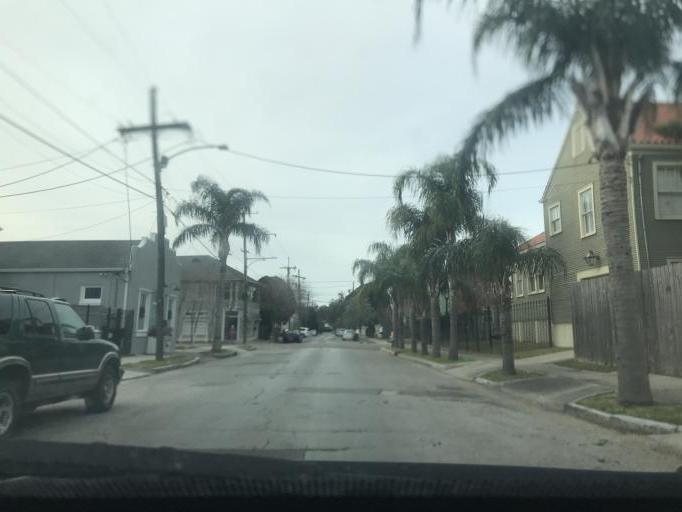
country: US
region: Louisiana
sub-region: Orleans Parish
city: New Orleans
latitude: 29.9564
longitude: -90.1120
